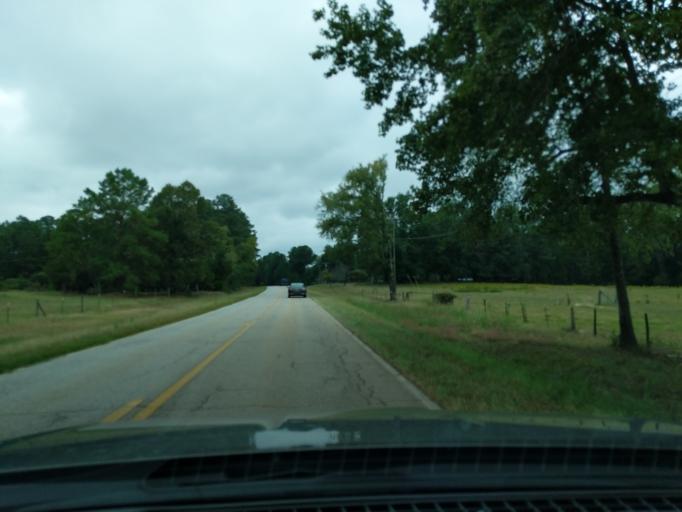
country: US
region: Georgia
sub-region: Columbia County
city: Appling
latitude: 33.6281
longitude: -82.4002
